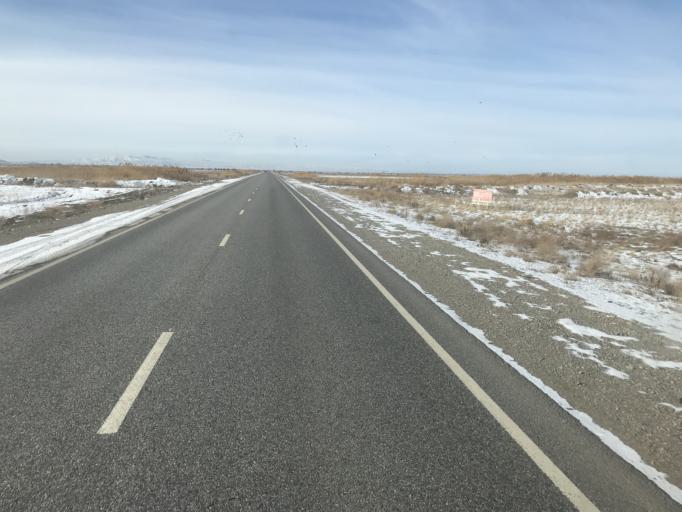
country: KZ
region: Zhambyl
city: Sarykemer
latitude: 43.0330
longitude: 71.3892
